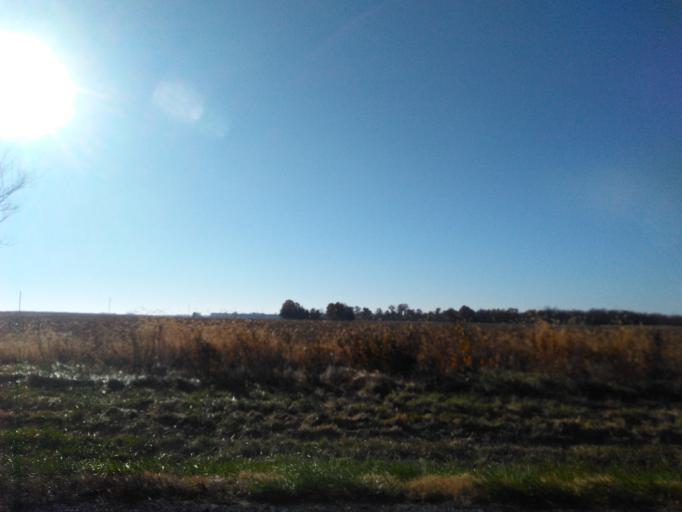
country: US
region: Illinois
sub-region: Madison County
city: Troy
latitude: 38.7559
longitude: -89.8522
